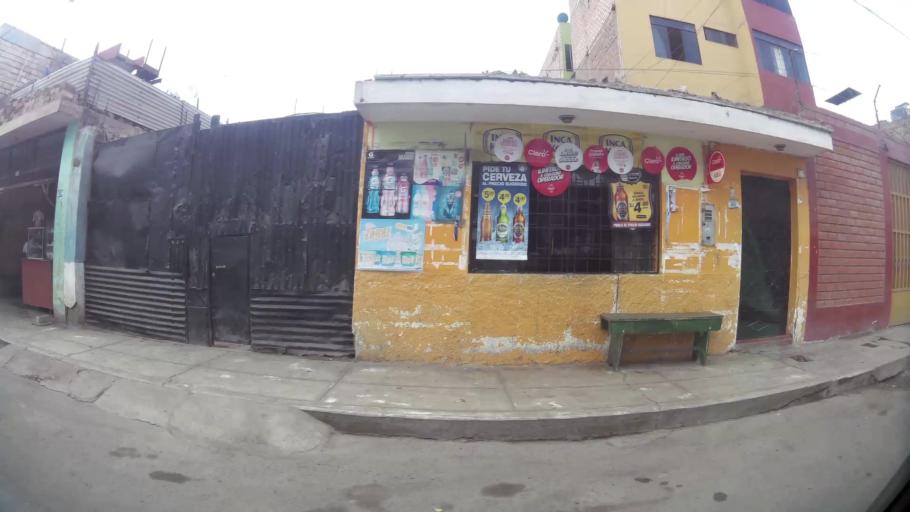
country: PE
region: Lima
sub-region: Provincia de Huaral
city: Huaral
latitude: -11.4923
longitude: -77.2098
